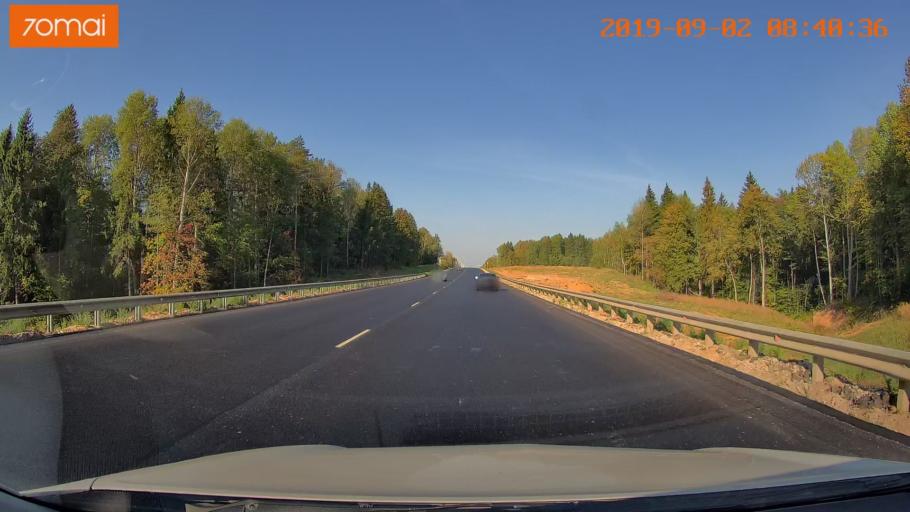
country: RU
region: Kaluga
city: Kudinovo
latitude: 54.9739
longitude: 36.1300
